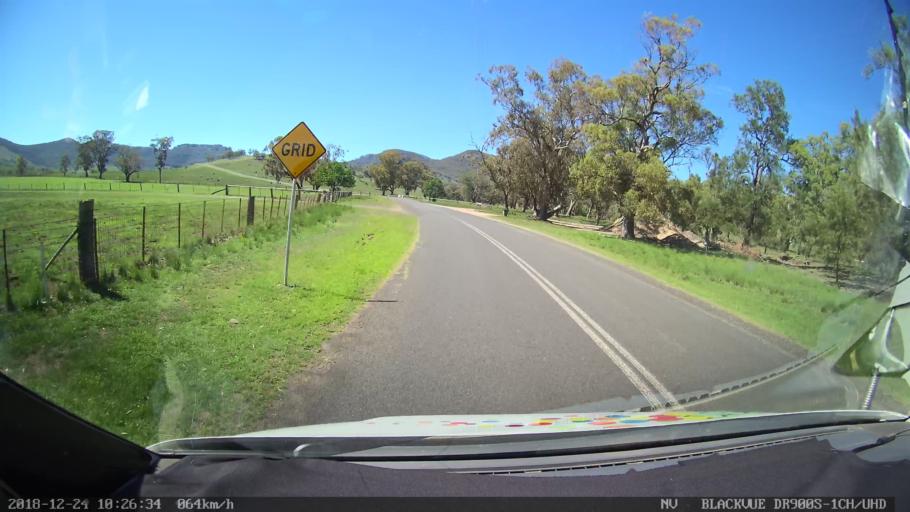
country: AU
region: New South Wales
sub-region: Liverpool Plains
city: Quirindi
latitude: -31.8105
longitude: 150.5272
